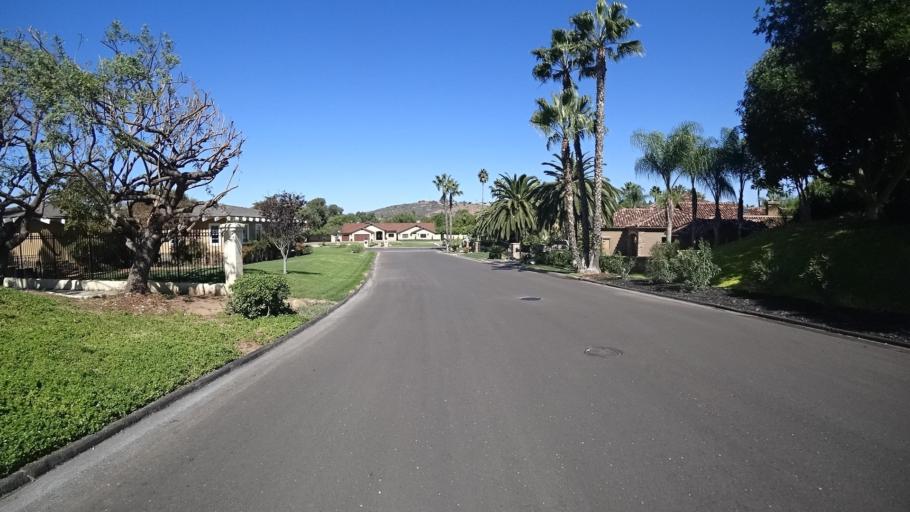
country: US
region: California
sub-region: San Diego County
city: Rancho San Diego
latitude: 32.7383
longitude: -116.9182
